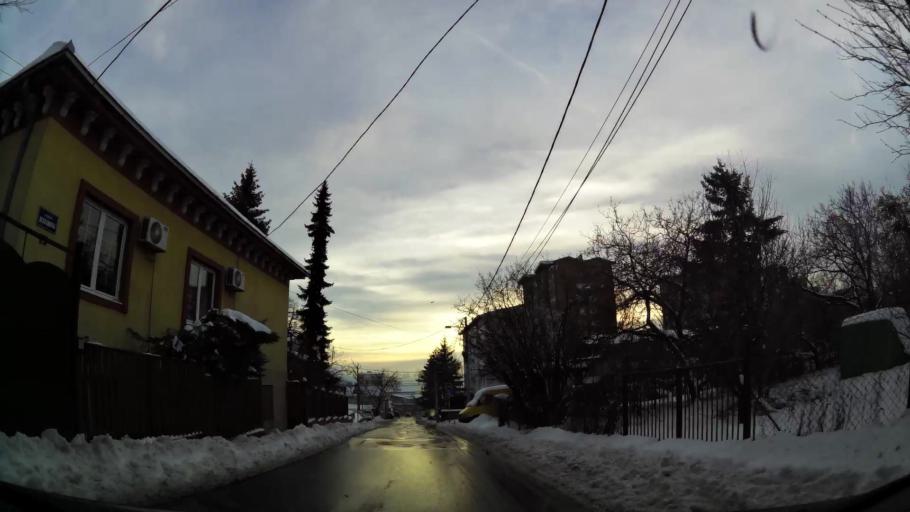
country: RS
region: Central Serbia
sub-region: Belgrade
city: Palilula
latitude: 44.7934
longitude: 20.5115
